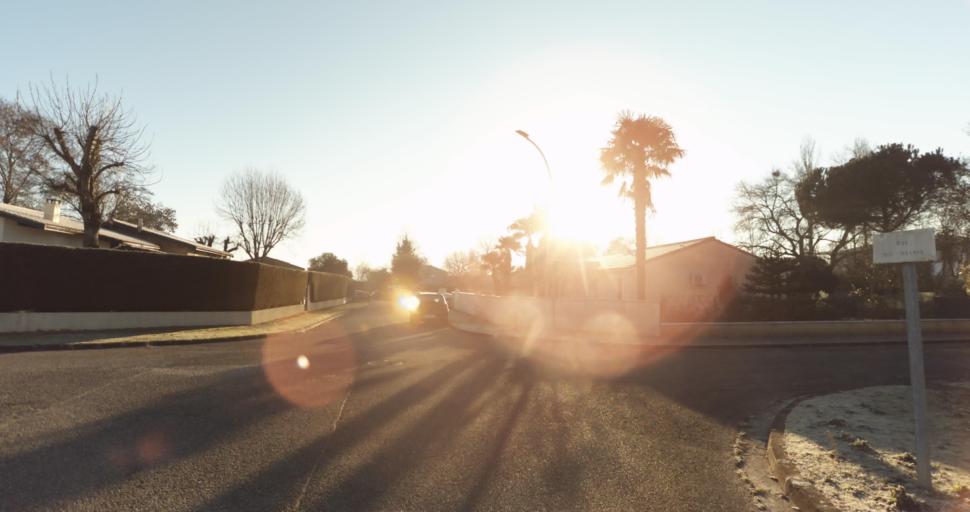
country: FR
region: Aquitaine
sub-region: Departement de la Gironde
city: Carbon-Blanc
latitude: 44.9018
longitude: -0.5015
